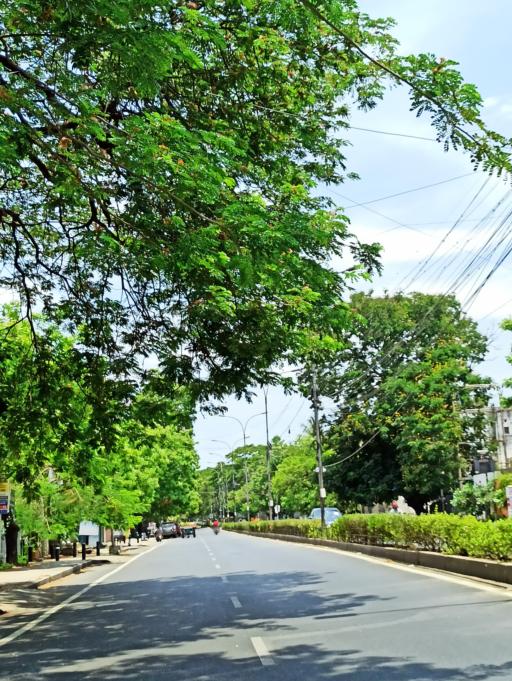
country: IN
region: Tamil Nadu
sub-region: Chennai
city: Chetput
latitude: 13.0824
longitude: 80.2059
